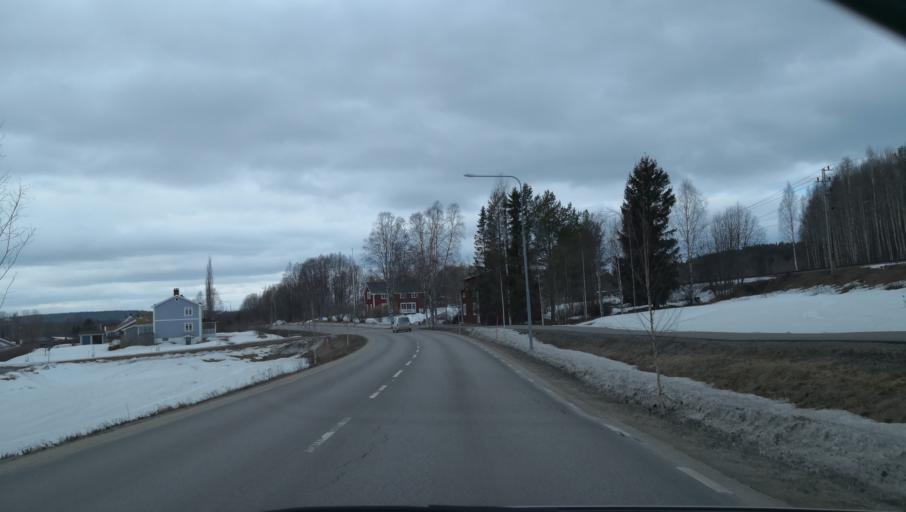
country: SE
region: Vaesterbotten
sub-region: Vannas Kommun
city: Vannasby
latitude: 63.9167
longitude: 19.8006
